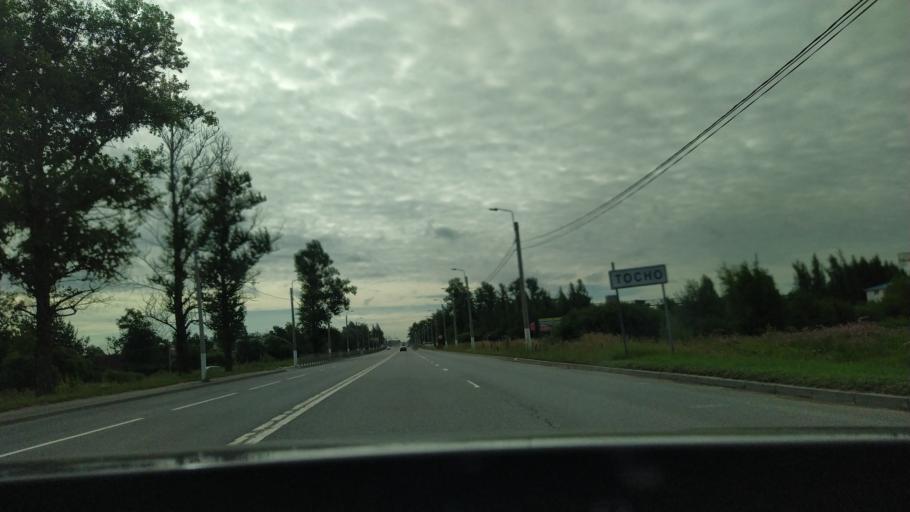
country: RU
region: Leningrad
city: Tosno
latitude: 59.5623
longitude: 30.8380
